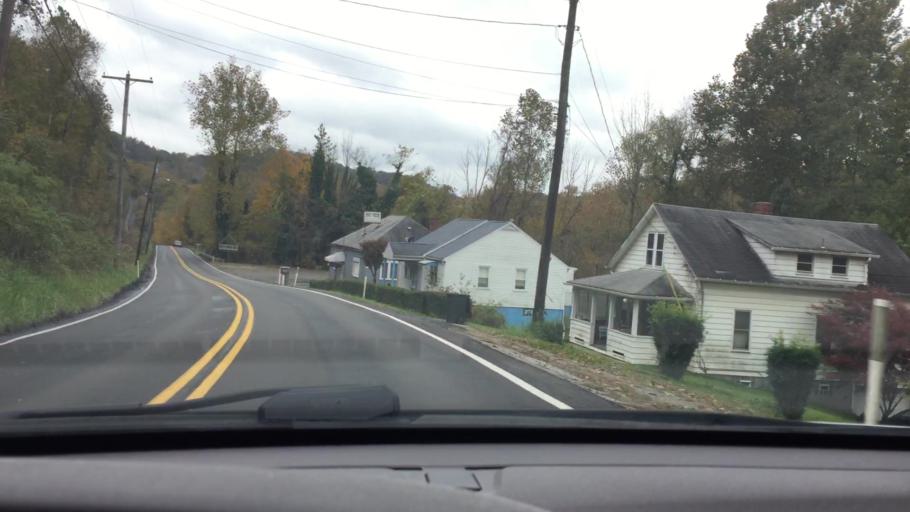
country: US
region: Pennsylvania
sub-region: Washington County
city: Speers
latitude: 40.1163
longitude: -79.8868
